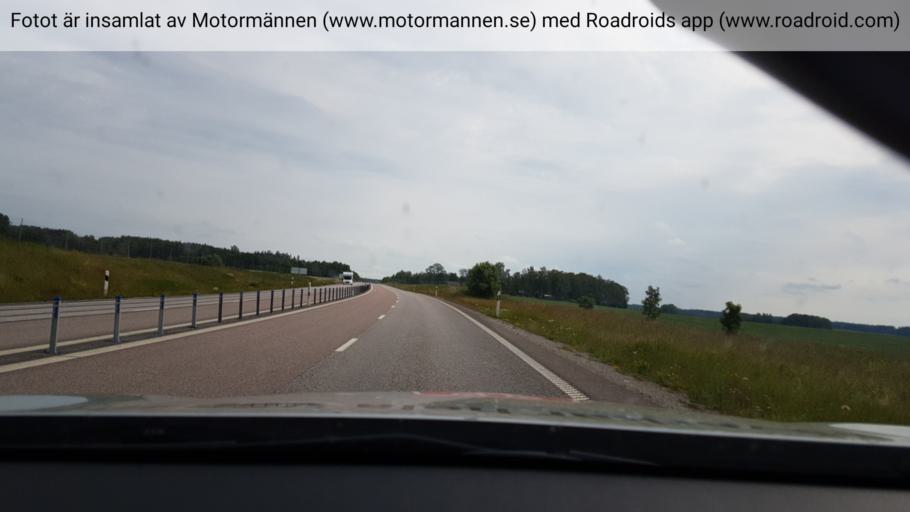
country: SE
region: Vaestra Goetaland
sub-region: Skovde Kommun
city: Skultorp
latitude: 58.3227
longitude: 13.8371
